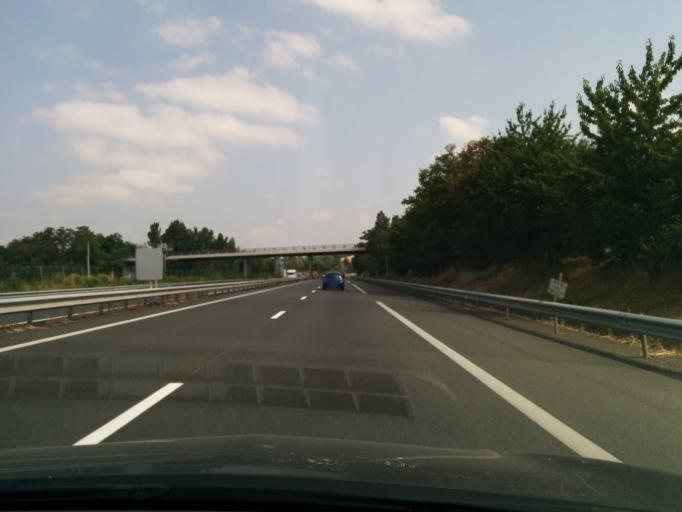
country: FR
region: Midi-Pyrenees
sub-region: Departement de la Haute-Garonne
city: Garidech
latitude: 43.6988
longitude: 1.5683
